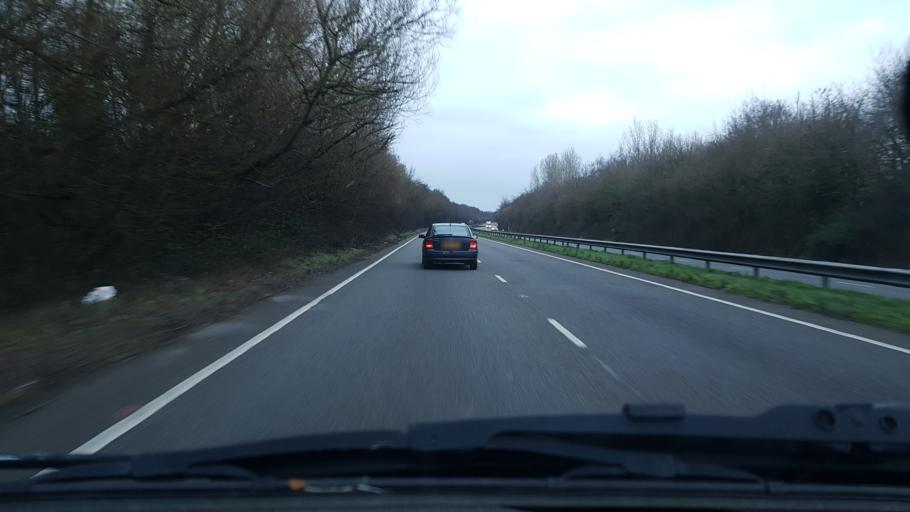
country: GB
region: England
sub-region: Hampshire
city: Farnborough
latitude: 51.2902
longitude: -0.7366
